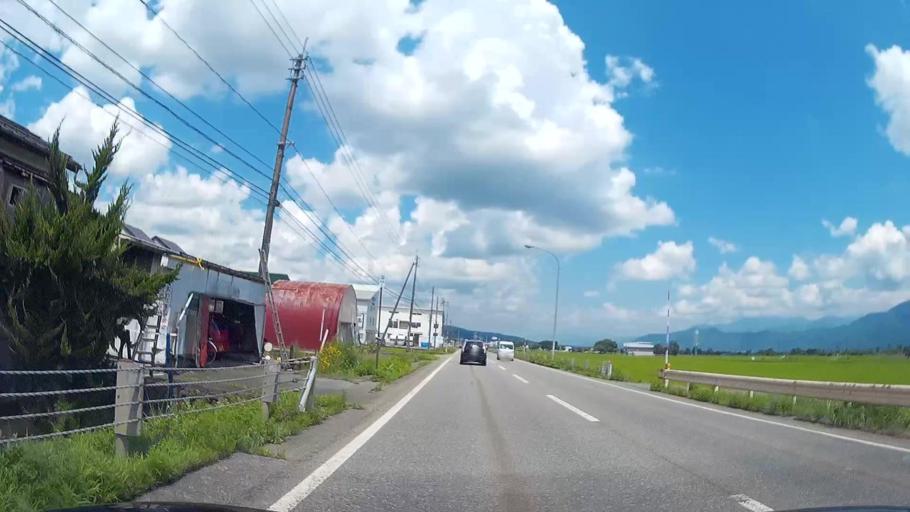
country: JP
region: Niigata
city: Shiozawa
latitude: 36.9984
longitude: 138.8143
